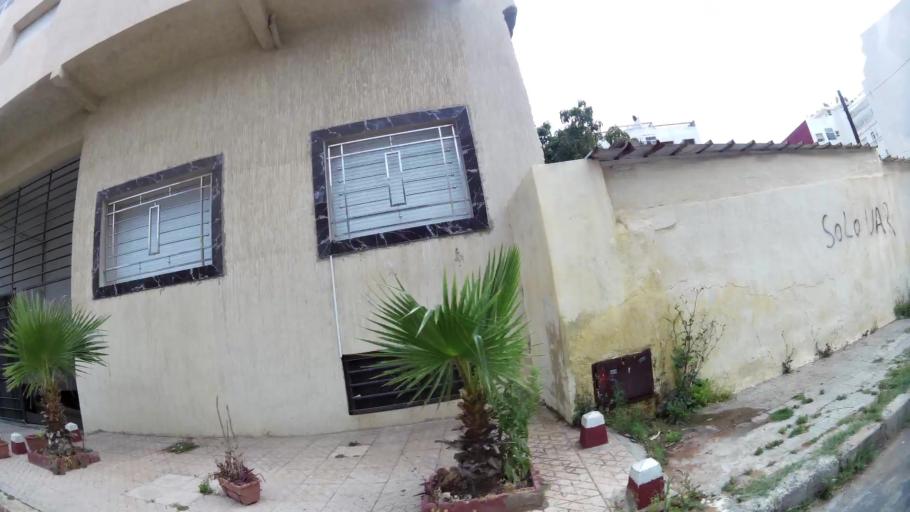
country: MA
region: Rabat-Sale-Zemmour-Zaer
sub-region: Rabat
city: Rabat
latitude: 34.0141
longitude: -6.8539
